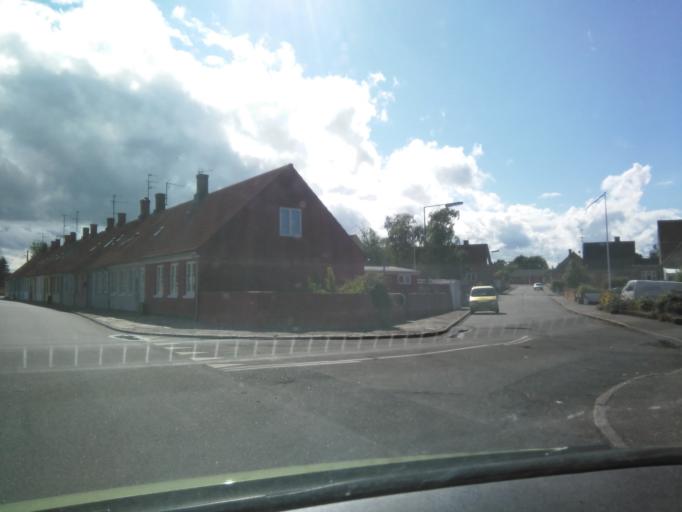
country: DK
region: Capital Region
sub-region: Bornholm Kommune
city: Nexo
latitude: 55.0610
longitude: 15.1278
